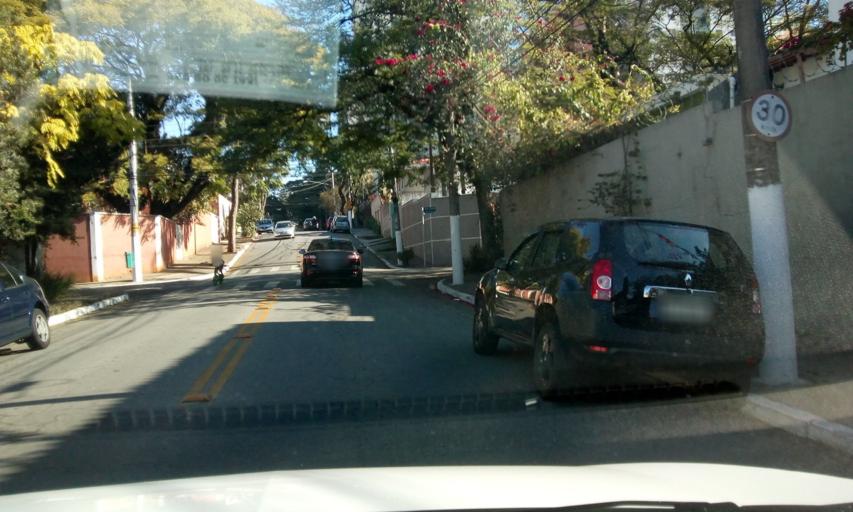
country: BR
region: Sao Paulo
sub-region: Sao Paulo
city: Sao Paulo
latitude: -23.6111
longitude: -46.6755
